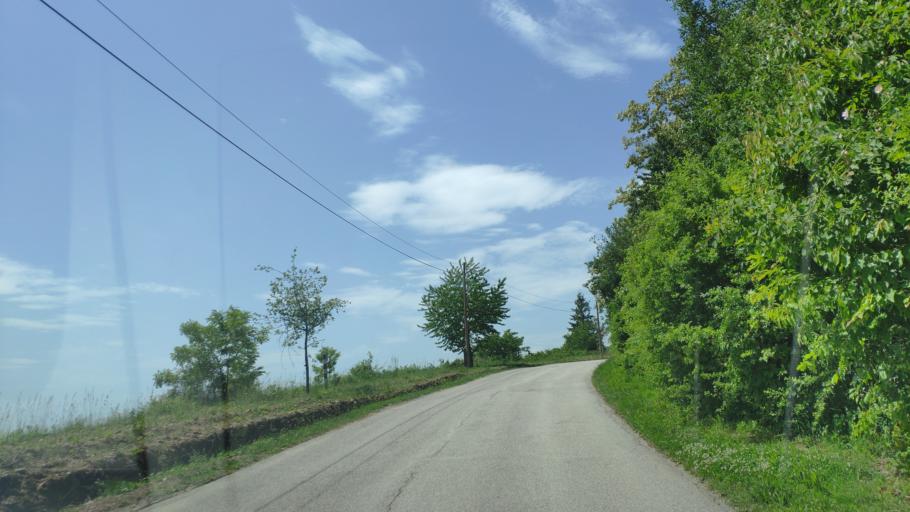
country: SK
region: Kosicky
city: Medzev
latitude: 48.7152
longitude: 20.9828
